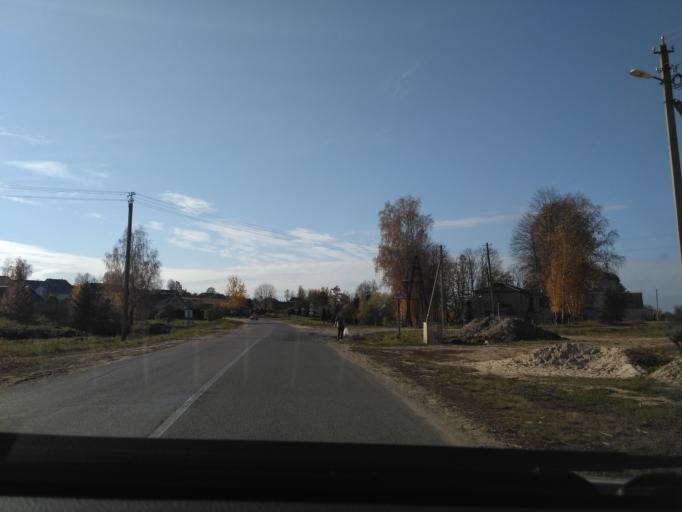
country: BY
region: Minsk
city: Loshnitsa
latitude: 54.3618
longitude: 28.6251
